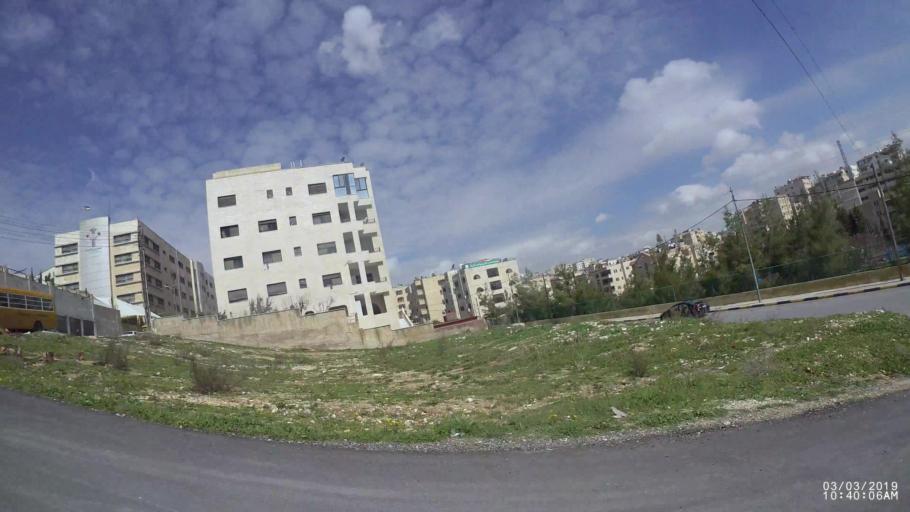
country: JO
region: Amman
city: Amman
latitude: 31.9907
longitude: 35.9075
